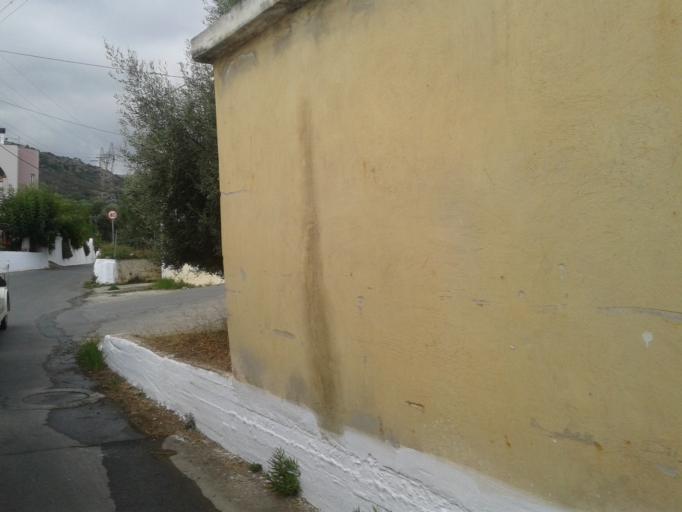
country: GR
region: Crete
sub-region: Nomos Chanias
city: Perivolia
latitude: 35.4795
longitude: 23.9935
